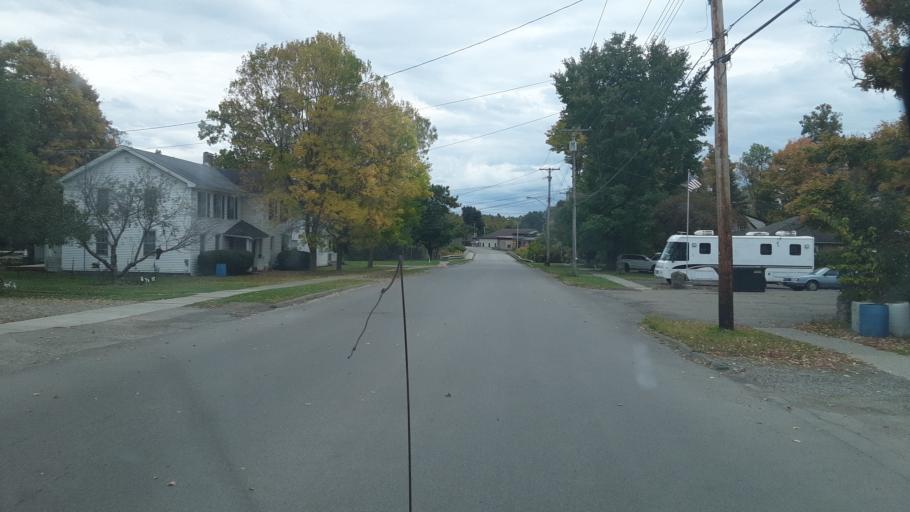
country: US
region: New York
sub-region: Allegany County
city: Belmont
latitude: 42.2276
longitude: -78.0329
